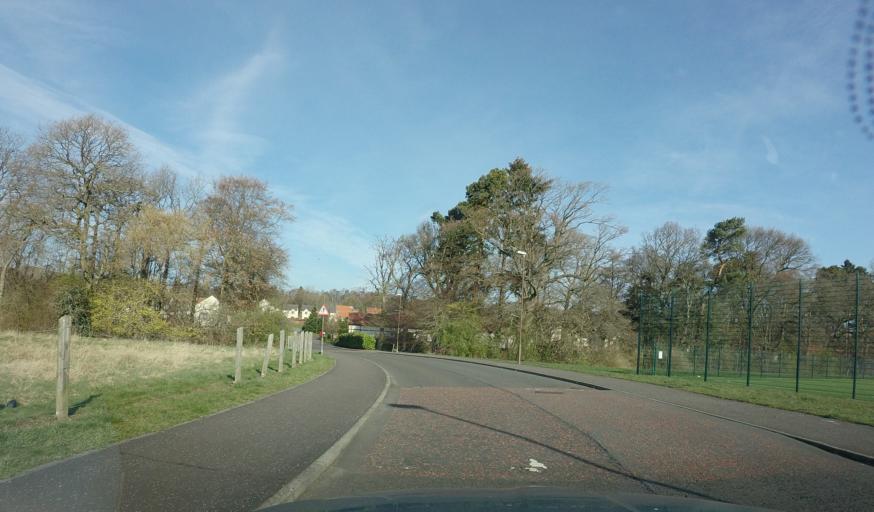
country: GB
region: Scotland
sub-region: Midlothian
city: Penicuik
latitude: 55.8487
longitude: -3.2065
